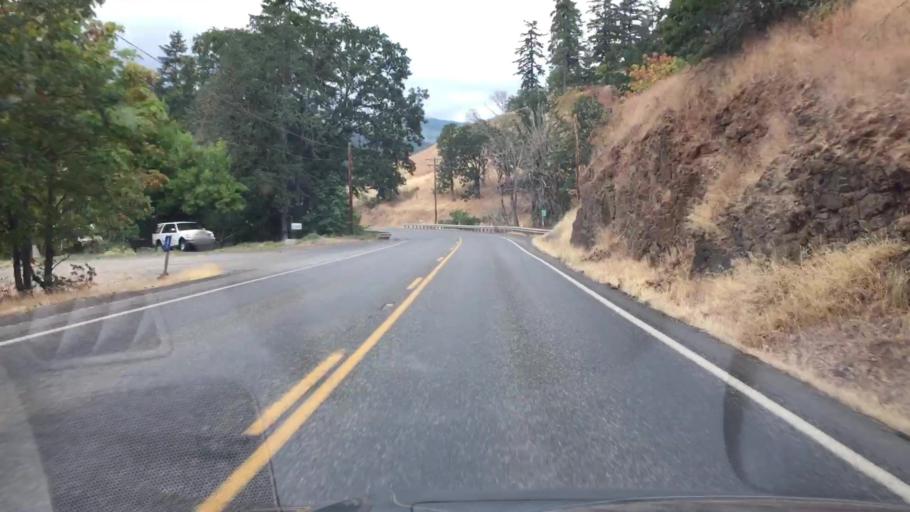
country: US
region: Washington
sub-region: Klickitat County
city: White Salmon
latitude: 45.7595
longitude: -121.5243
